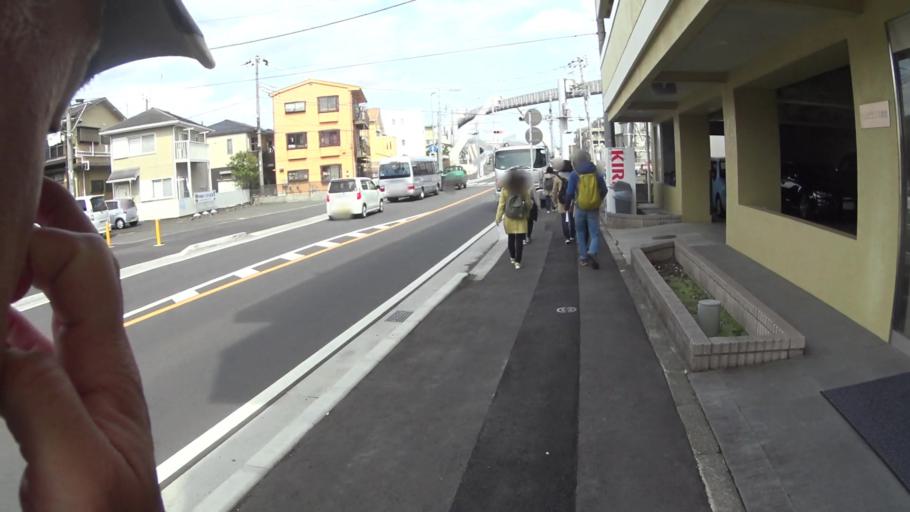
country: JP
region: Kanagawa
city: Kamakura
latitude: 35.3456
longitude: 139.5289
